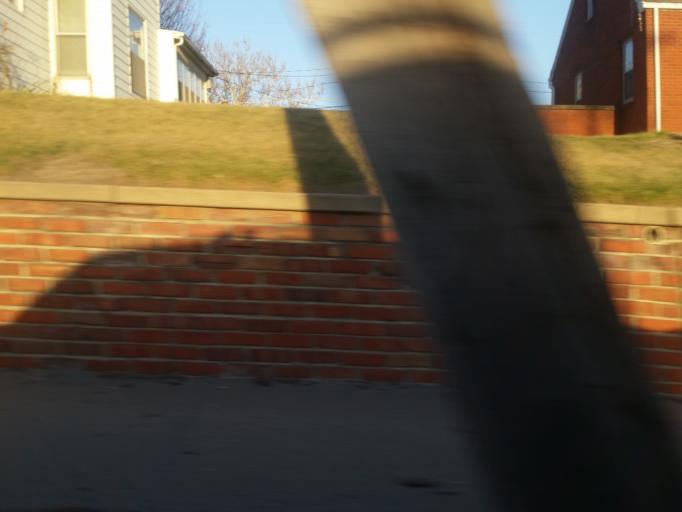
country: US
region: Nebraska
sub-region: Douglas County
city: Omaha
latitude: 41.2327
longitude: -95.9332
